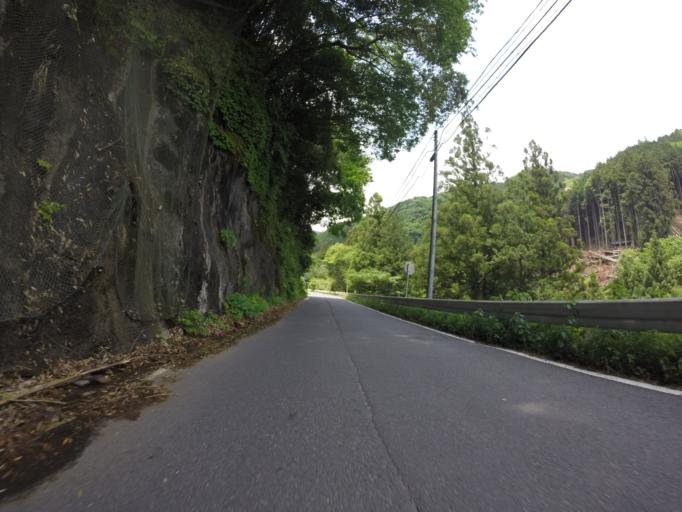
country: JP
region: Shizuoka
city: Shizuoka-shi
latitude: 35.1184
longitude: 138.3045
